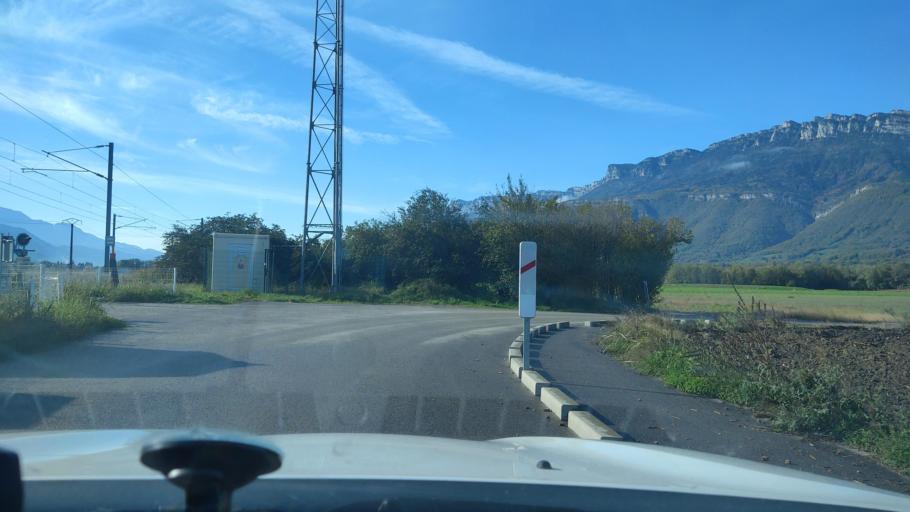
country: FR
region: Rhone-Alpes
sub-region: Departement de l'Isere
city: Pontcharra
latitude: 45.4563
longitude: 6.0238
